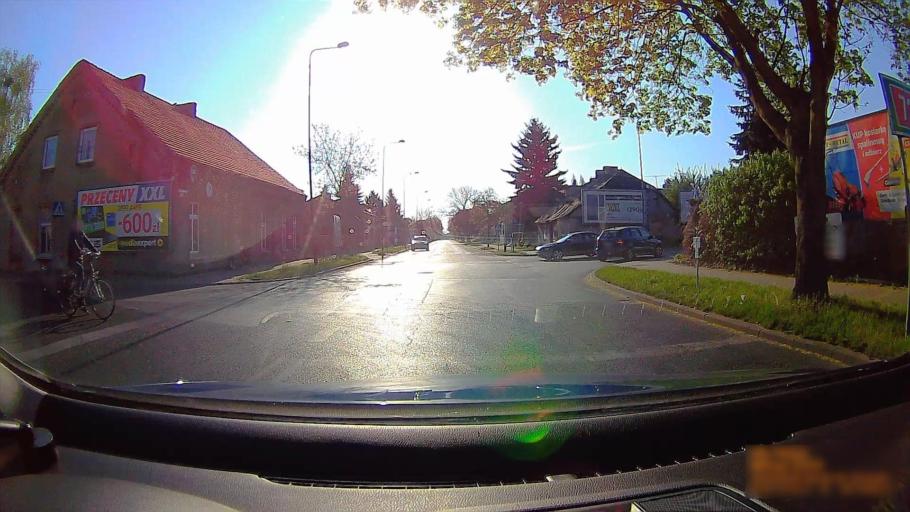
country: PL
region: Greater Poland Voivodeship
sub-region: Konin
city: Konin
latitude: 52.2040
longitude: 18.2621
